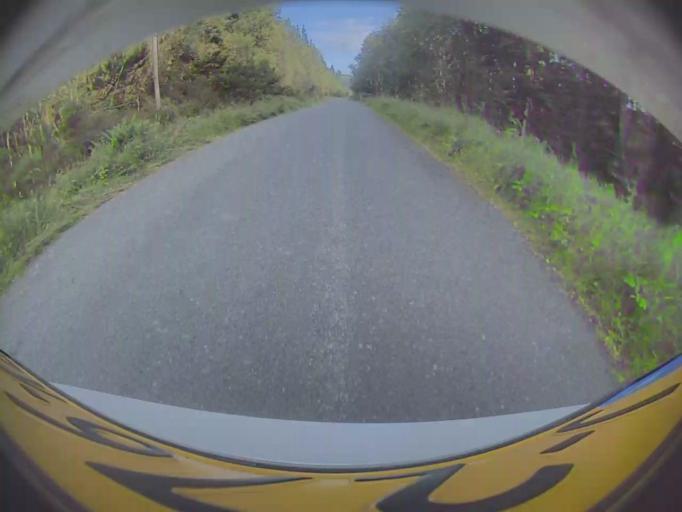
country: IE
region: Leinster
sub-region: Wicklow
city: Rathdrum
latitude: 53.0155
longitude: -6.3004
